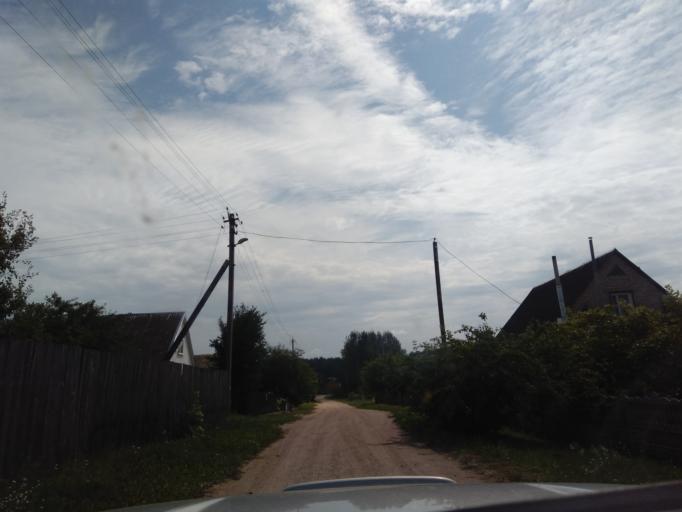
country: BY
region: Minsk
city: Kapyl'
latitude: 53.1595
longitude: 27.0975
